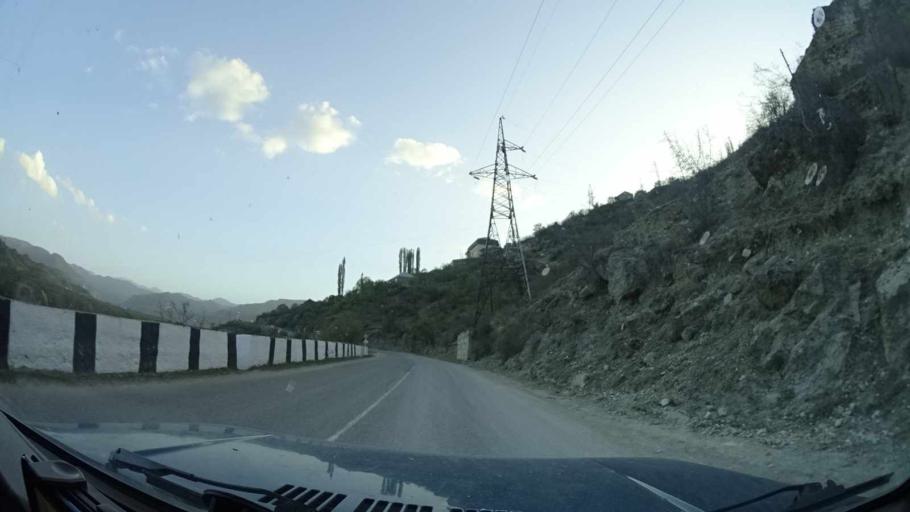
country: RU
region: Dagestan
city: Gunib
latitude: 42.3837
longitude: 46.9672
